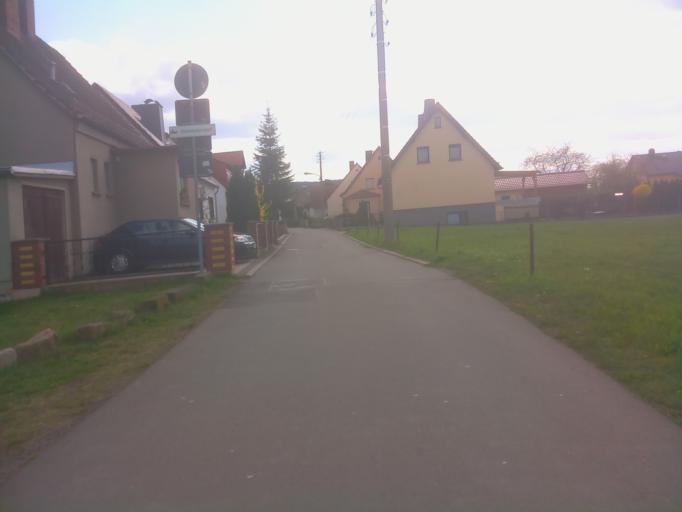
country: DE
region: Thuringia
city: Kleineutersdorf
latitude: 50.7906
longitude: 11.5790
